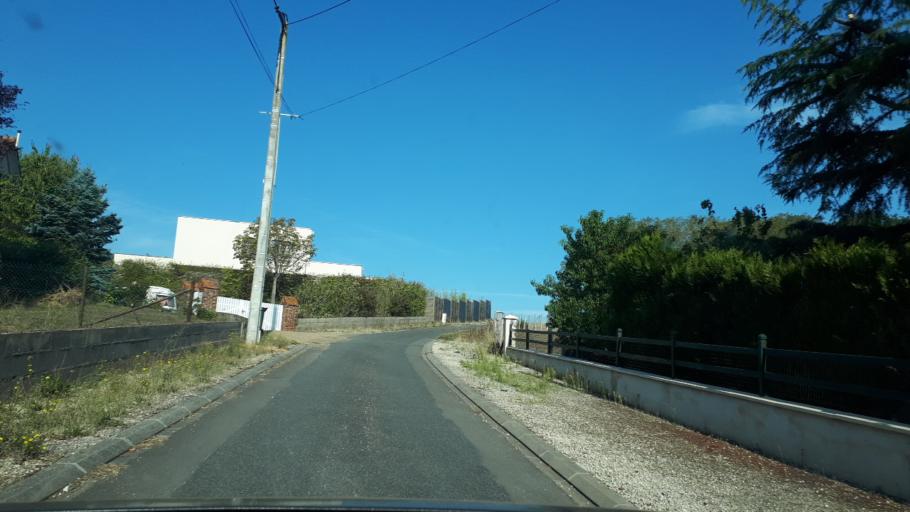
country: FR
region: Centre
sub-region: Departement du Loir-et-Cher
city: Aze
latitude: 47.8349
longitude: 0.9829
